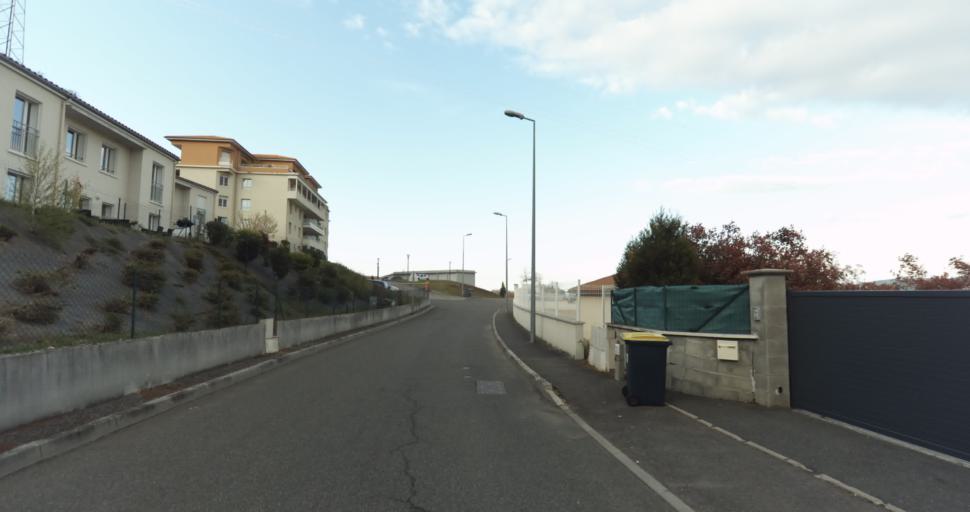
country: FR
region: Rhone-Alpes
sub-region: Departement de la Loire
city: Saint-Jean-Bonnefonds
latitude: 45.4481
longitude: 4.4454
